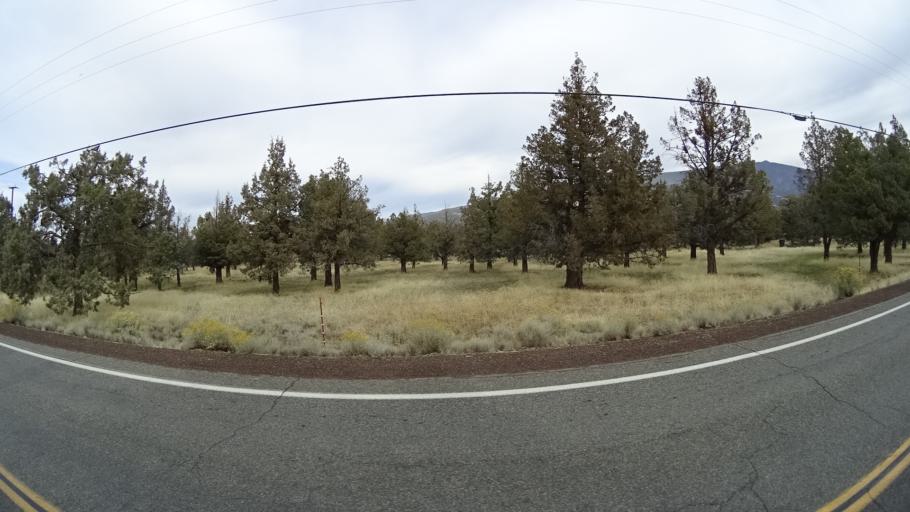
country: US
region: California
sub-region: Siskiyou County
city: Weed
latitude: 41.5927
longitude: -122.3094
